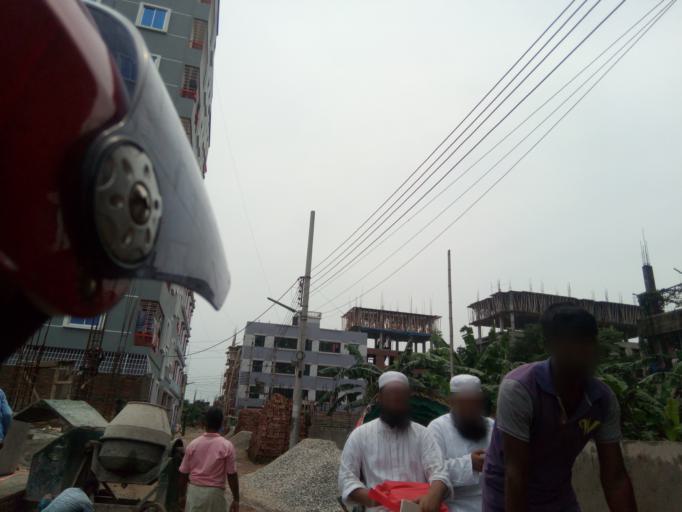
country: BD
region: Dhaka
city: Azimpur
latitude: 23.7436
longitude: 90.3501
